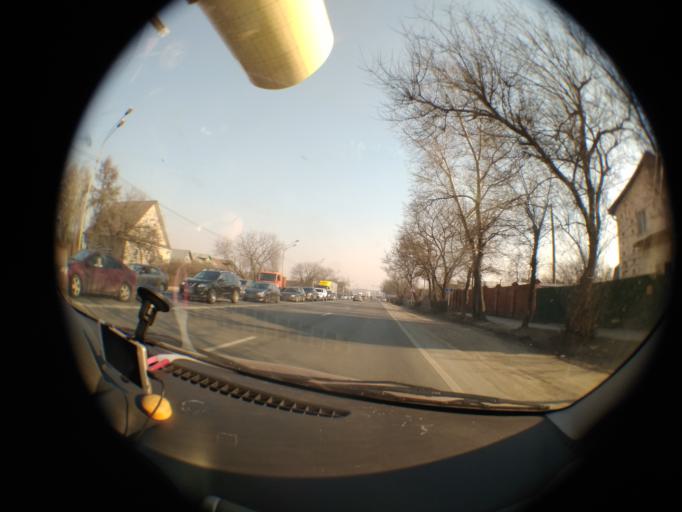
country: RU
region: Moskovskaya
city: Ostrovtsy
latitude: 55.5864
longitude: 38.0097
